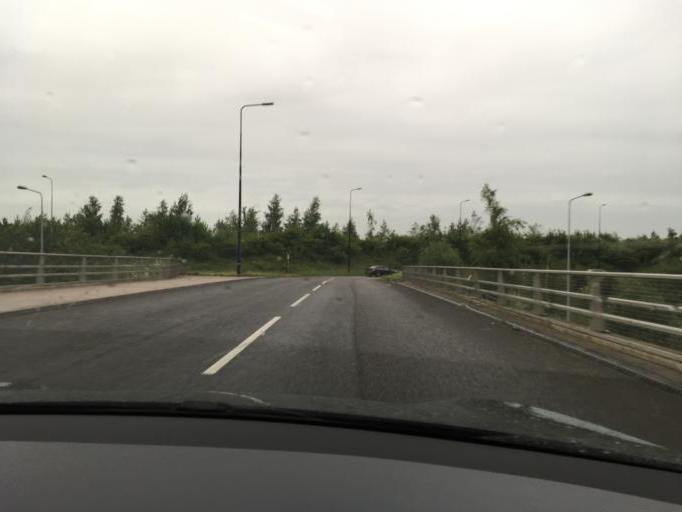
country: GB
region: England
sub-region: Trafford
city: Sale
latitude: 53.4410
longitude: -2.3359
